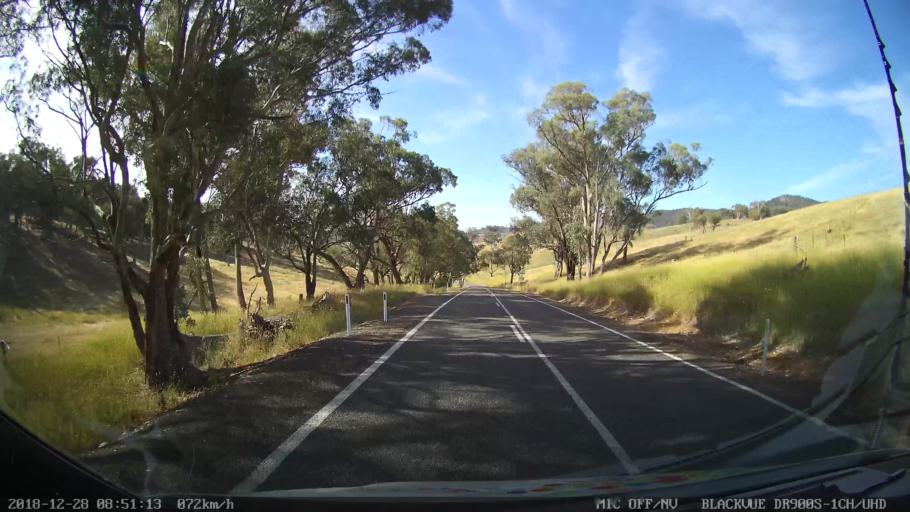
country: AU
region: New South Wales
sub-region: Upper Lachlan Shire
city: Crookwell
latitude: -34.0657
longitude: 149.3395
